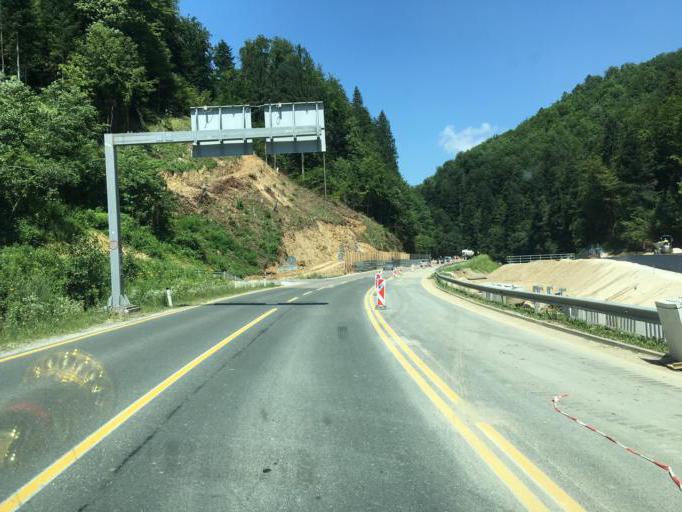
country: SI
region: Zetale
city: Zetale
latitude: 46.2788
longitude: 15.8623
